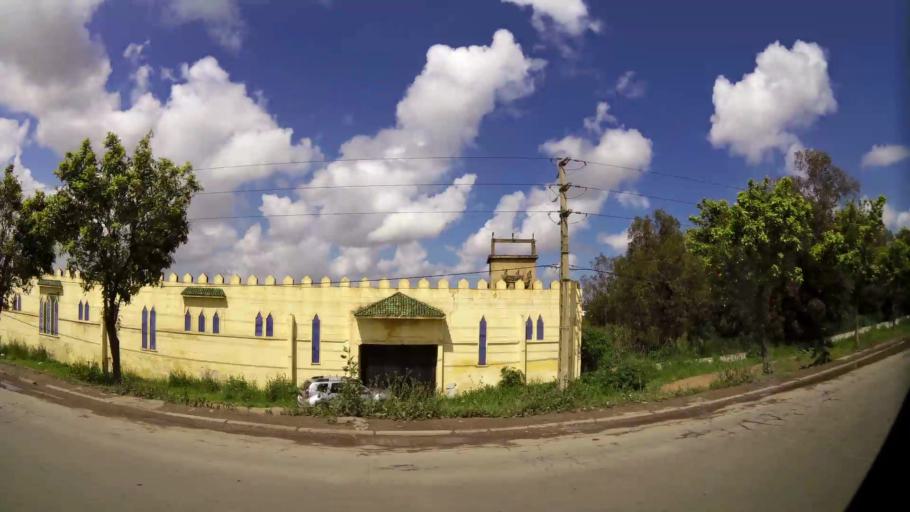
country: MA
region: Grand Casablanca
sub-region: Mediouna
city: Tit Mellil
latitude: 33.5562
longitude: -7.4868
